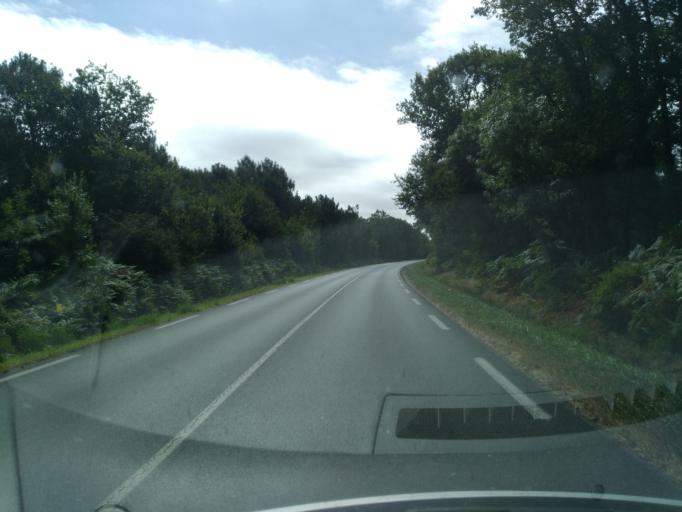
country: FR
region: Poitou-Charentes
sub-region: Departement de la Charente-Maritime
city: Chaillevette
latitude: 45.7172
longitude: -1.0707
